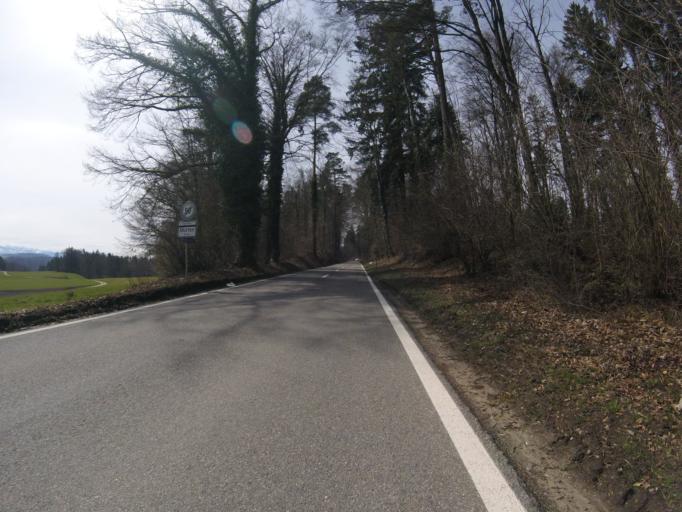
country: CH
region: Fribourg
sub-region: Sense District
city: Bosingen
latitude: 46.9081
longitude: 7.2139
